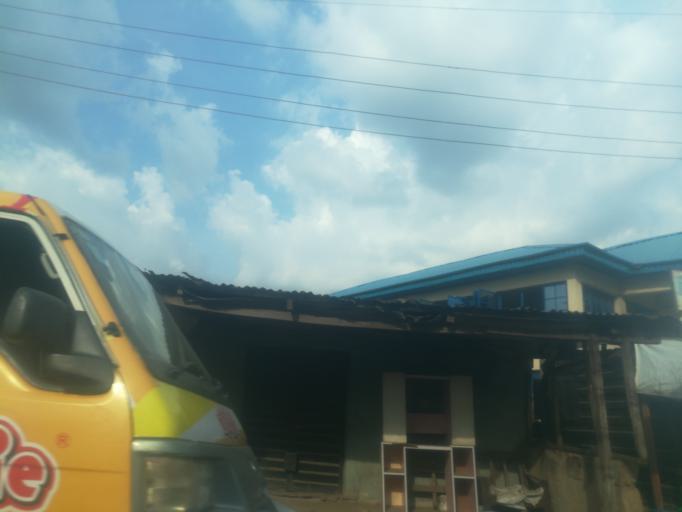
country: NG
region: Ogun
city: Abeokuta
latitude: 7.1450
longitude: 3.3272
